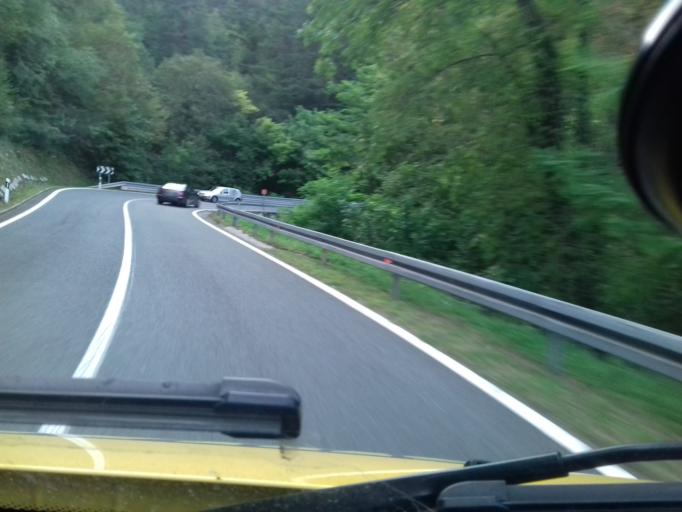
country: BA
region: Federation of Bosnia and Herzegovina
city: Ostrozac
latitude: 44.9015
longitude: 15.9366
